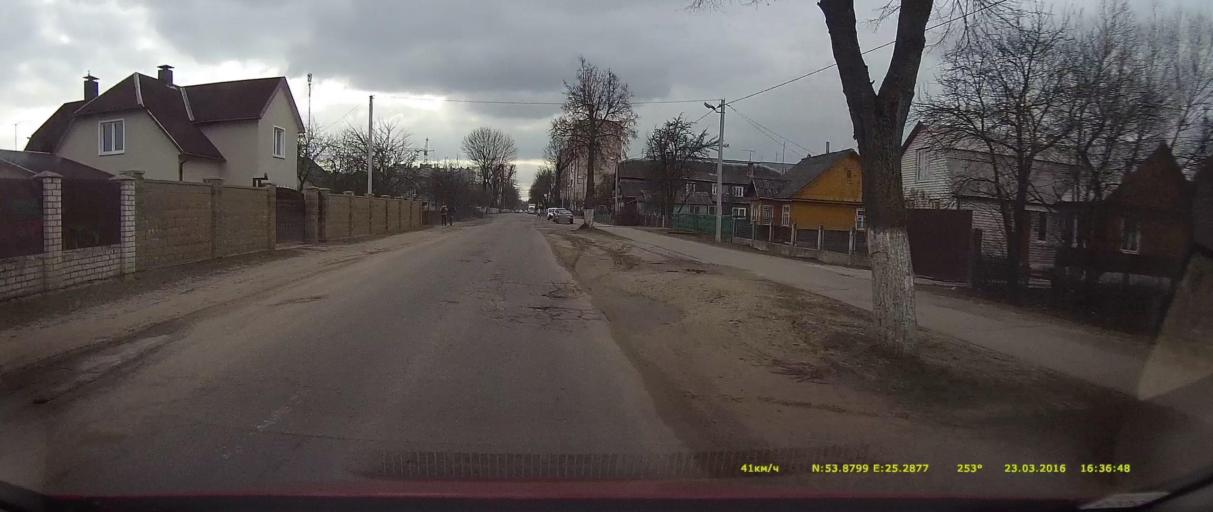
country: BY
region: Grodnenskaya
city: Lida
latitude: 53.8798
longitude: 25.2877
